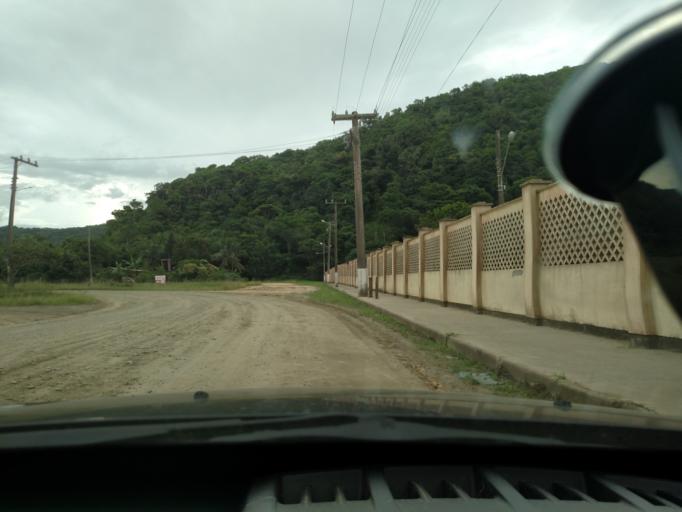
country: BR
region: Santa Catarina
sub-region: Porto Belo
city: Porto Belo
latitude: -27.1694
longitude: -48.5012
